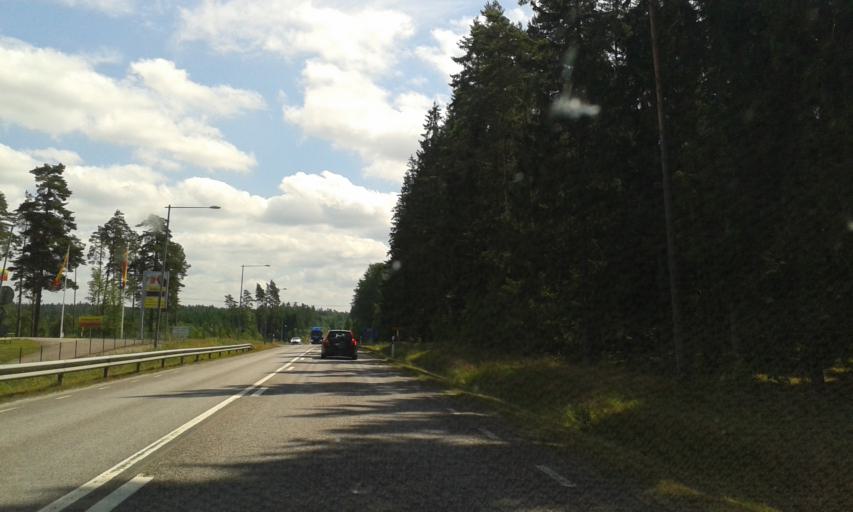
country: SE
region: Joenkoeping
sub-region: Varnamo Kommun
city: Rydaholm
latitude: 56.9749
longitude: 14.3143
